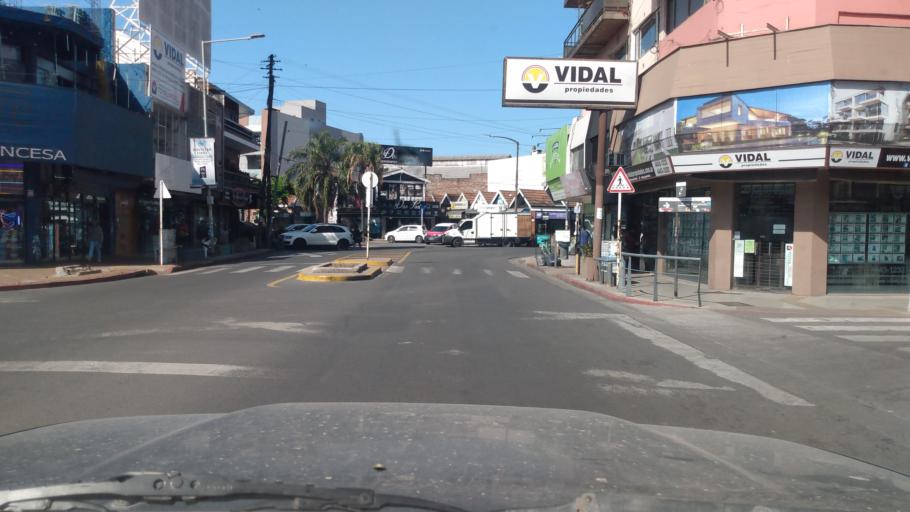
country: AR
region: Buenos Aires
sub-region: Partido de Moron
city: Moron
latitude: -34.6454
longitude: -58.5906
